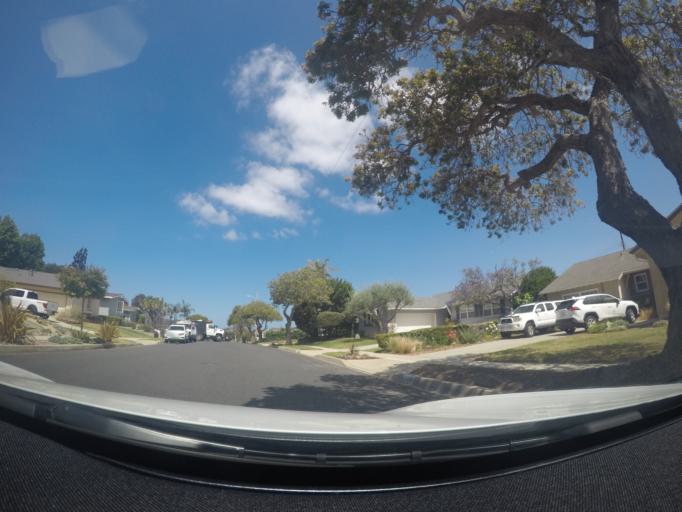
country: US
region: California
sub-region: Los Angeles County
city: Palos Verdes Estates
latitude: 33.8059
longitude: -118.3707
